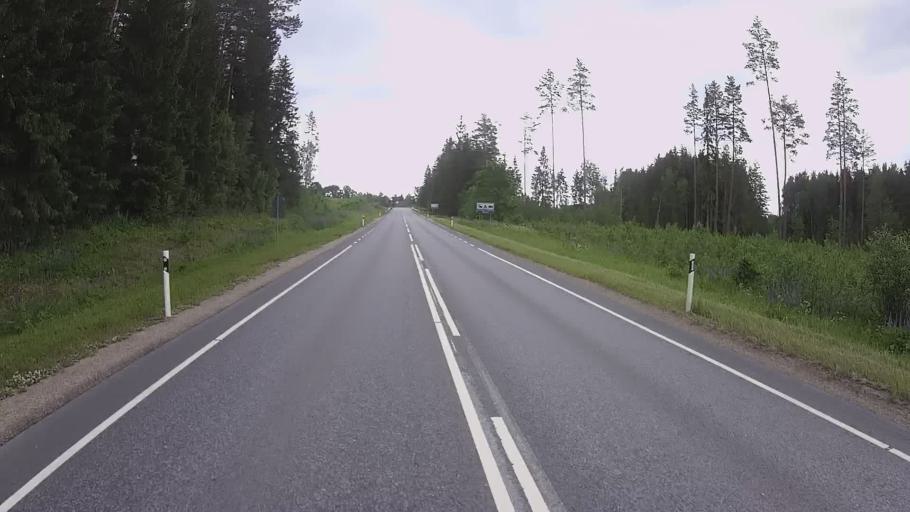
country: EE
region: Polvamaa
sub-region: Polva linn
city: Polva
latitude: 58.0977
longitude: 27.0011
